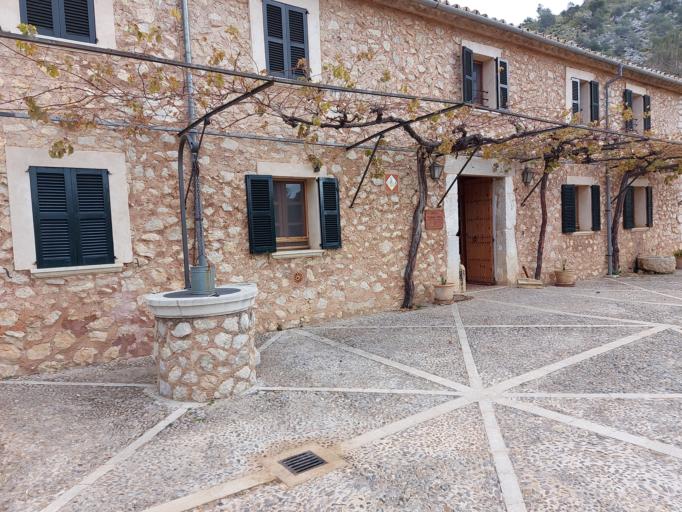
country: ES
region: Balearic Islands
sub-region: Illes Balears
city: Mancor de la Vall
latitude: 39.7687
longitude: 2.8190
